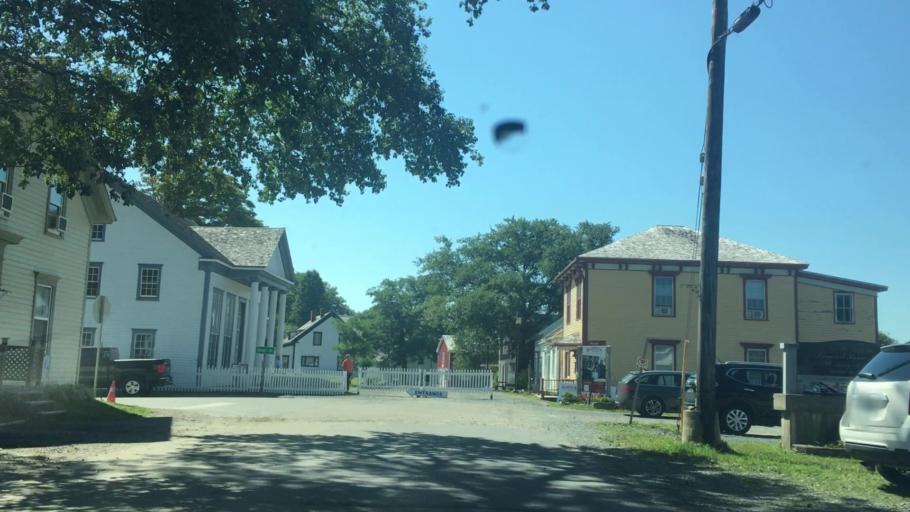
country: CA
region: Nova Scotia
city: Antigonish
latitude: 45.1412
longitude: -61.9838
